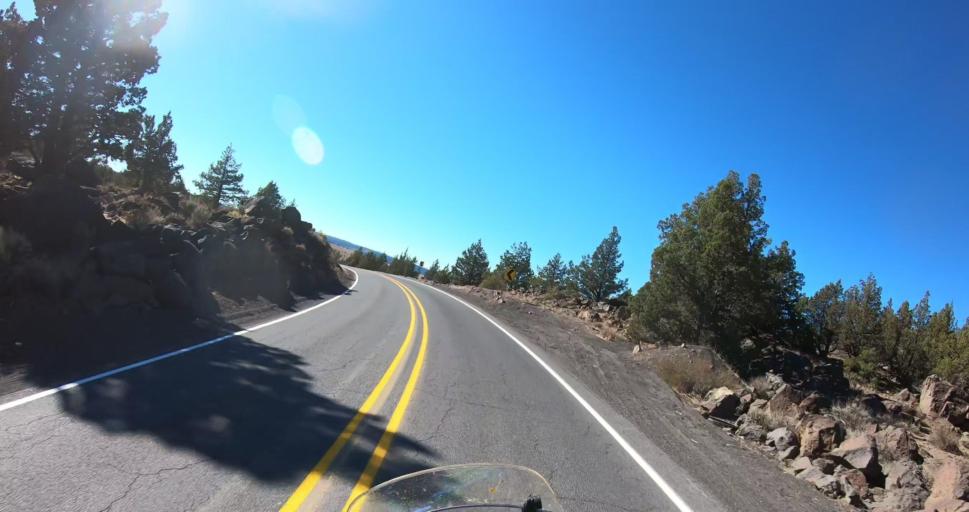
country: US
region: Oregon
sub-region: Deschutes County
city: La Pine
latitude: 43.0481
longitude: -120.7998
